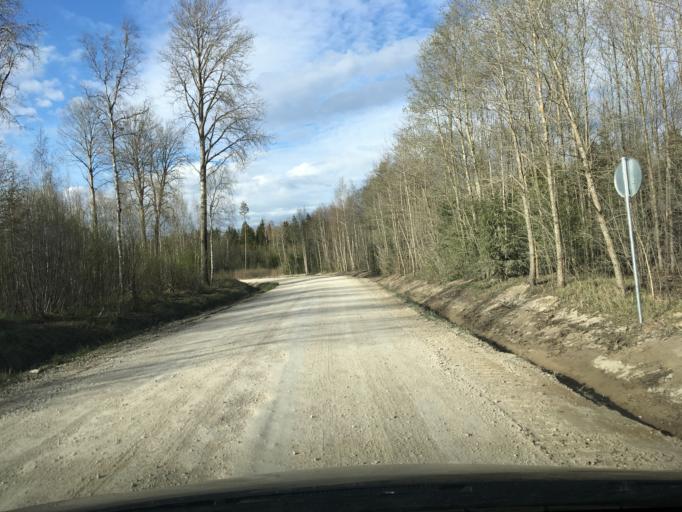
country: EE
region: Raplamaa
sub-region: Maerjamaa vald
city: Marjamaa
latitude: 58.9876
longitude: 24.3649
